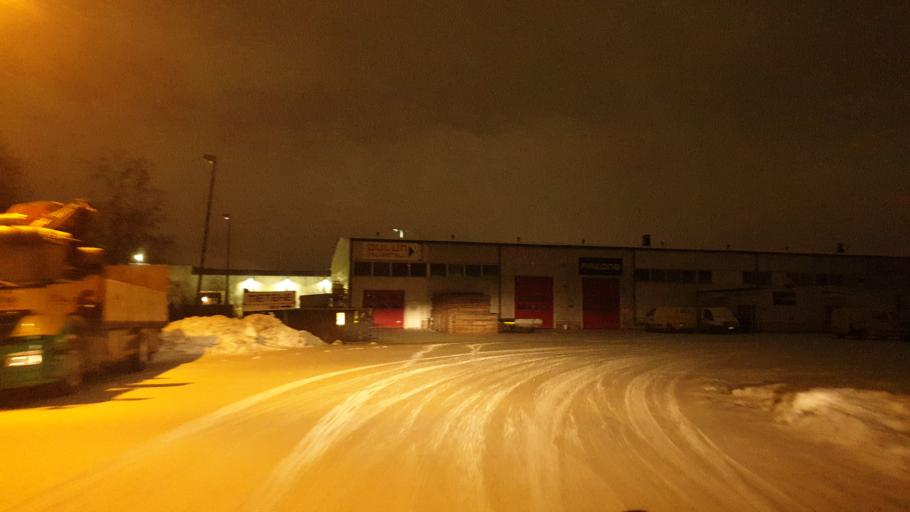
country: FI
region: Northern Ostrobothnia
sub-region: Oulu
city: Oulu
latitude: 64.9933
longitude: 25.4534
